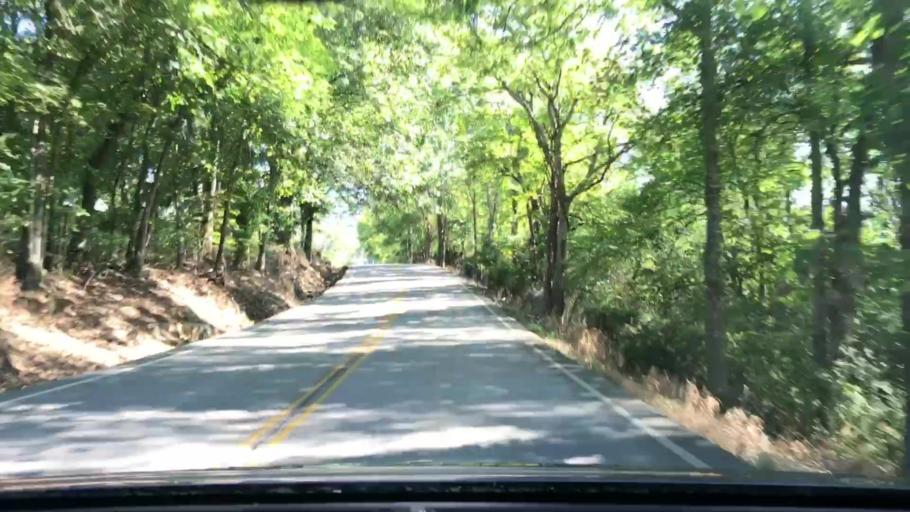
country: US
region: Tennessee
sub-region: Smith County
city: Carthage
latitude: 36.2773
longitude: -85.9502
